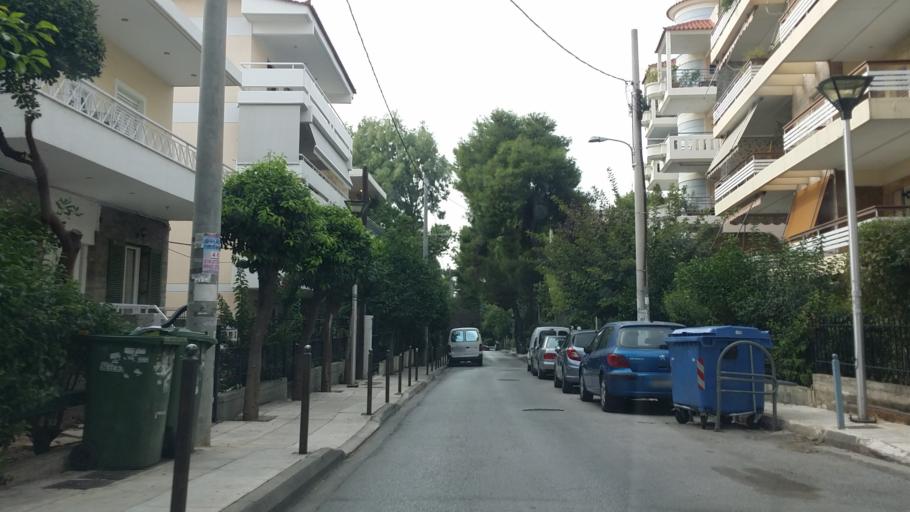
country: GR
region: Attica
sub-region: Nomarchia Athinas
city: Irakleio
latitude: 38.0475
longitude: 23.7693
